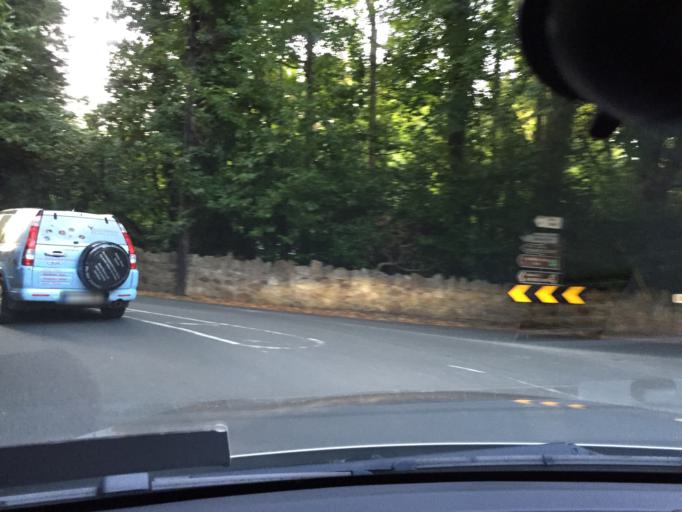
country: IE
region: Leinster
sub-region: Wicklow
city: Enniskerry
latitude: 53.1814
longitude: -6.1717
